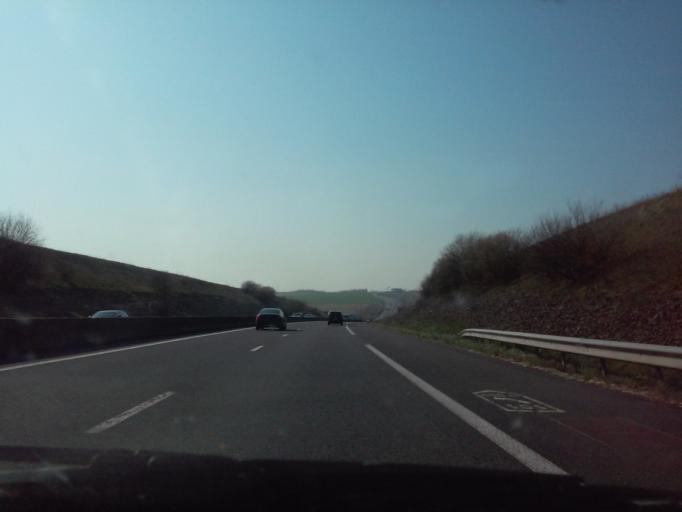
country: FR
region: Lower Normandy
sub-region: Departement du Calvados
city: Saint-Vigor-le-Grand
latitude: 49.2481
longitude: -0.6265
